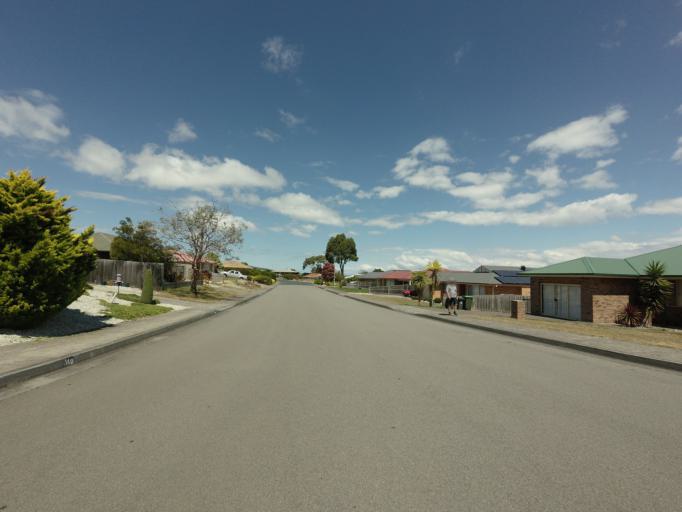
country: AU
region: Tasmania
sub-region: Clarence
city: Rokeby
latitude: -42.8984
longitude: 147.4565
